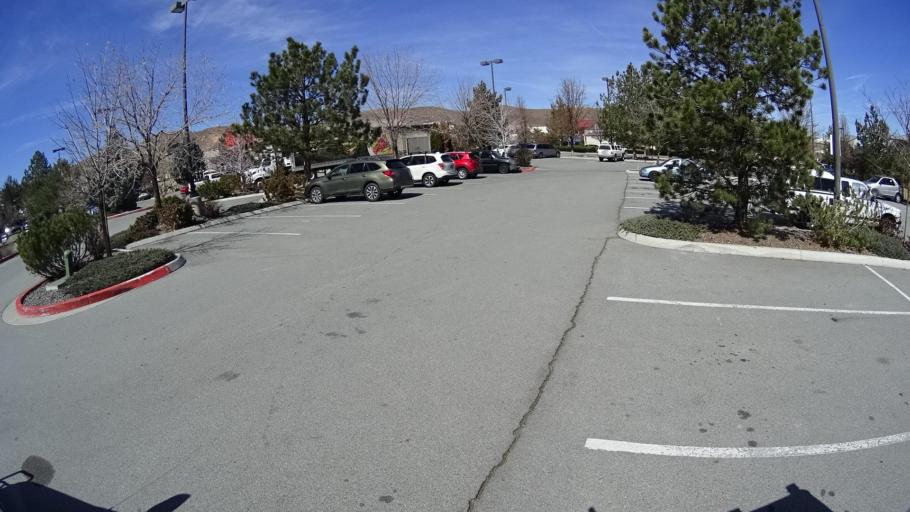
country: US
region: Nevada
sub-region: Washoe County
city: Sun Valley
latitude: 39.5769
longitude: -119.7392
